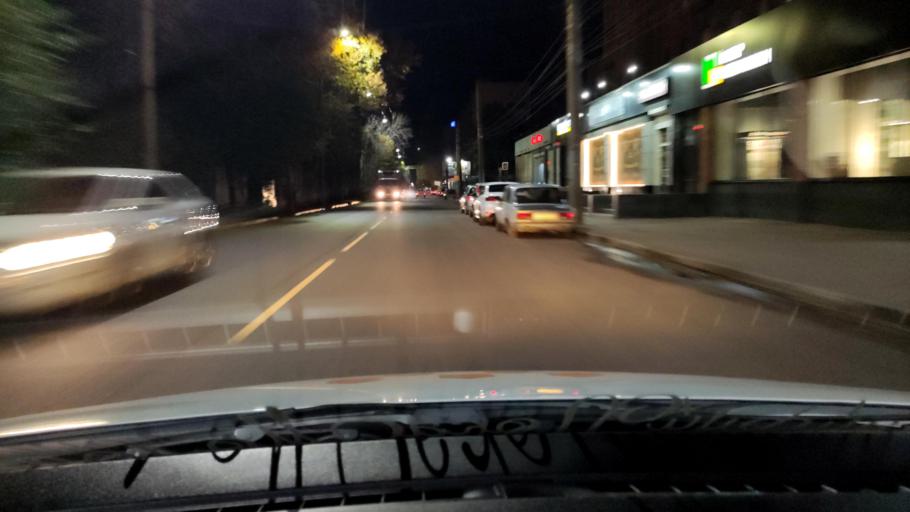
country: RU
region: Voronezj
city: Voronezh
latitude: 51.7031
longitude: 39.1907
